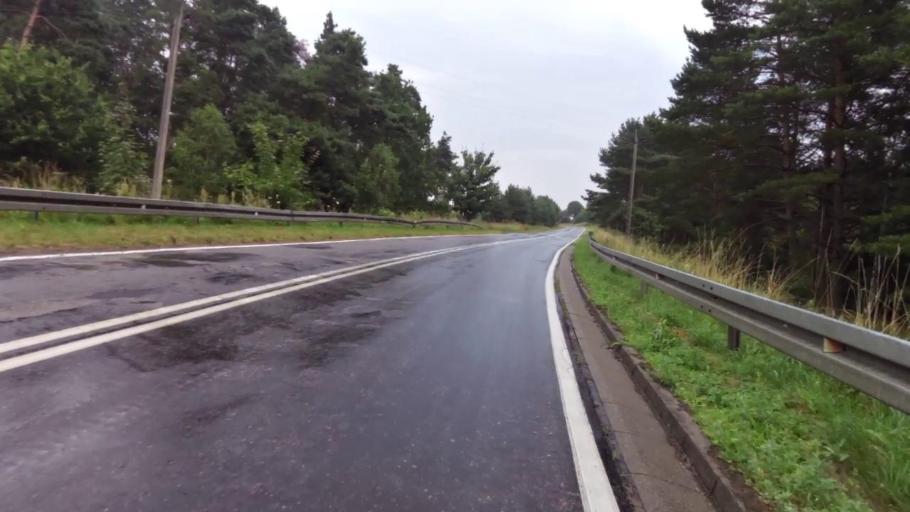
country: PL
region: West Pomeranian Voivodeship
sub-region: Powiat stargardzki
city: Insko
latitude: 53.4464
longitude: 15.5665
